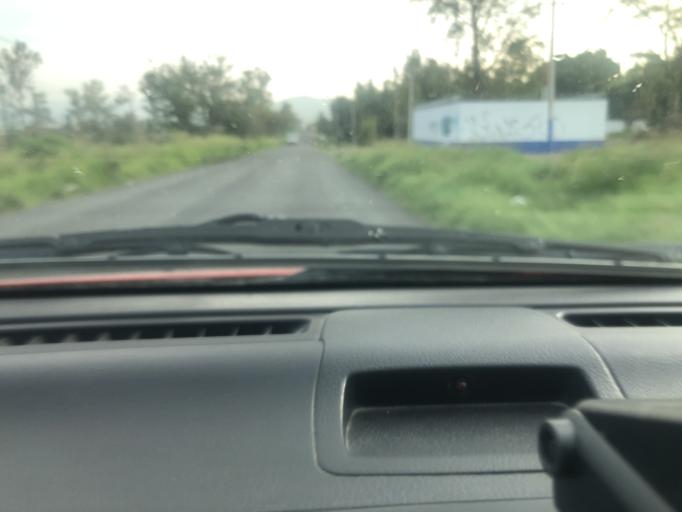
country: MX
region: Jalisco
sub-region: San Pedro Tlaquepaque
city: Paseo del Prado
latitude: 20.5713
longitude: -103.4065
